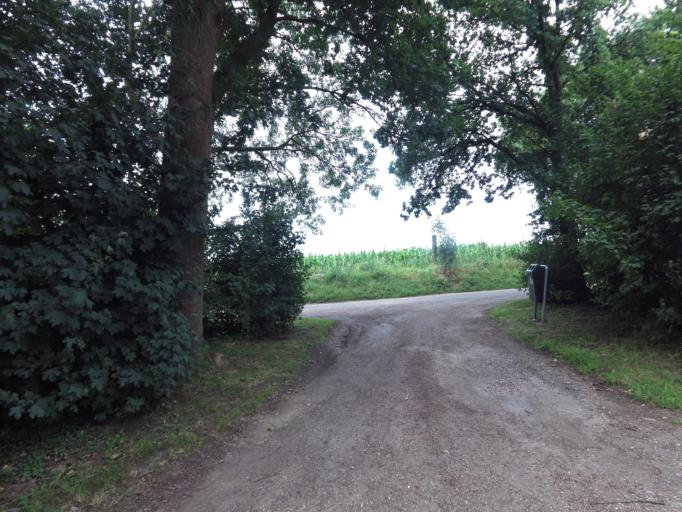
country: NL
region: Limburg
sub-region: Valkenburg aan de Geul
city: Schin op Geul
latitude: 50.8661
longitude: 5.8652
